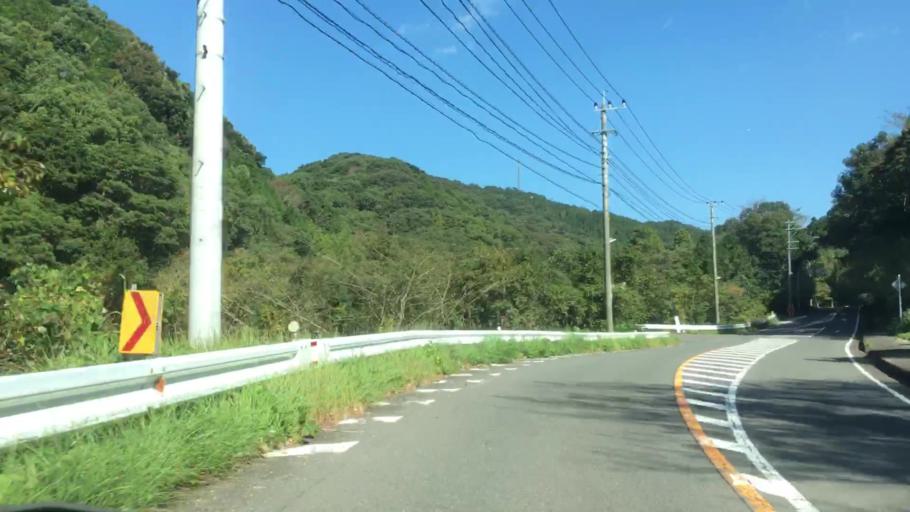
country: JP
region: Nagasaki
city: Sasebo
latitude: 33.0261
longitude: 129.6532
